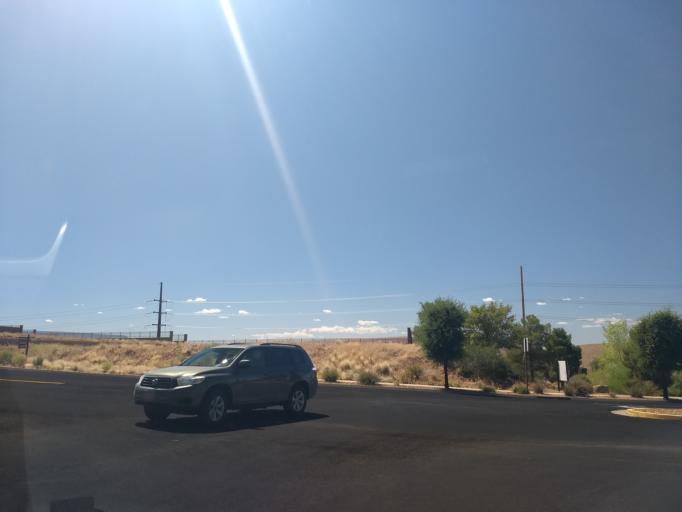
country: US
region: Utah
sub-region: Washington County
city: Washington
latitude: 37.1397
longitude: -113.4685
